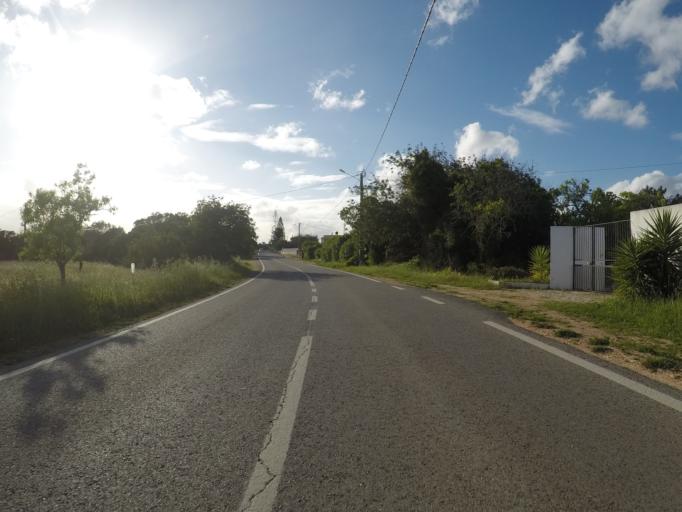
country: PT
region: Faro
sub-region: Lagoa
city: Carvoeiro
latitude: 37.0927
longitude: -8.4307
